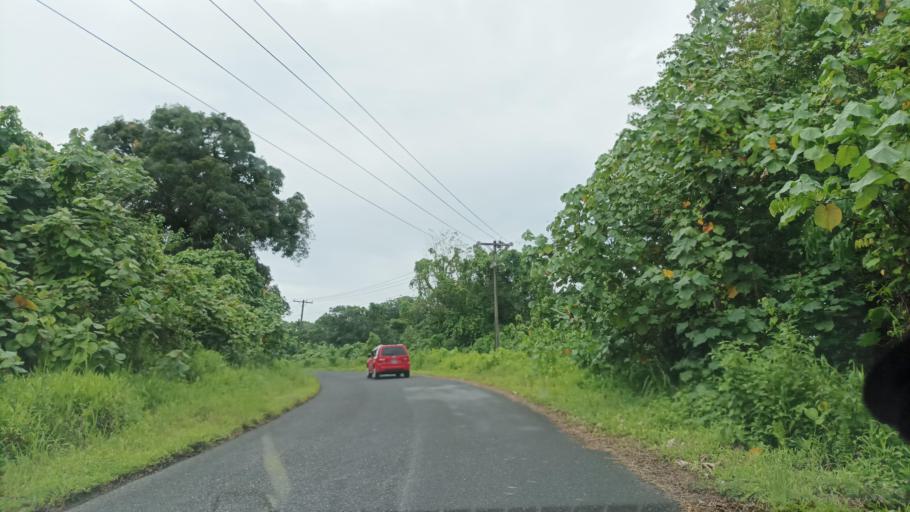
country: FM
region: Pohnpei
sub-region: Madolenihm Municipality
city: Madolenihm Municipality Government
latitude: 6.8959
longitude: 158.3106
